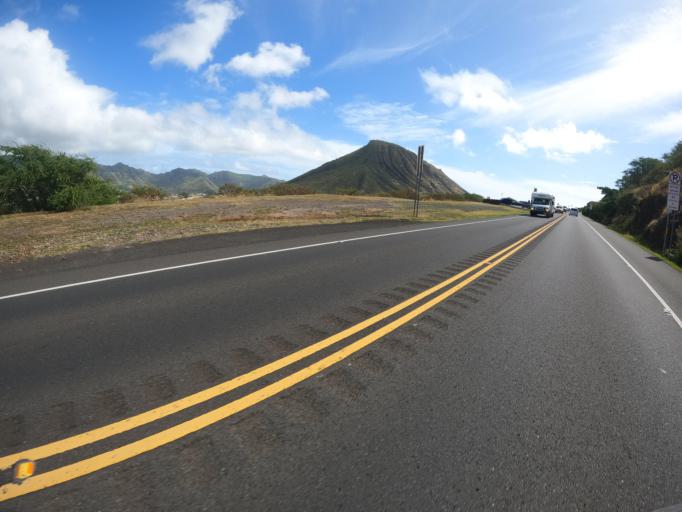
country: US
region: Hawaii
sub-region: Honolulu County
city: Waimanalo Beach
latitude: 21.2751
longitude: -157.6961
